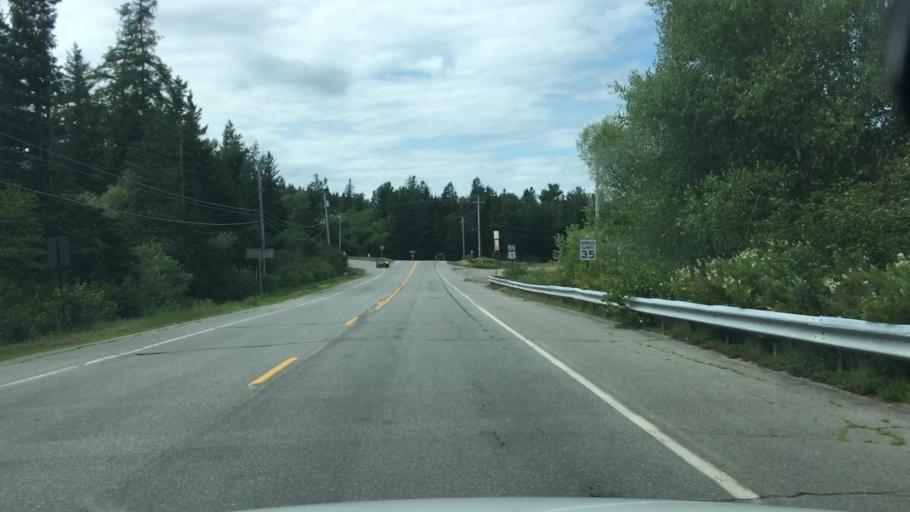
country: US
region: Maine
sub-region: Washington County
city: Eastport
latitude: 44.9694
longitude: -67.0731
